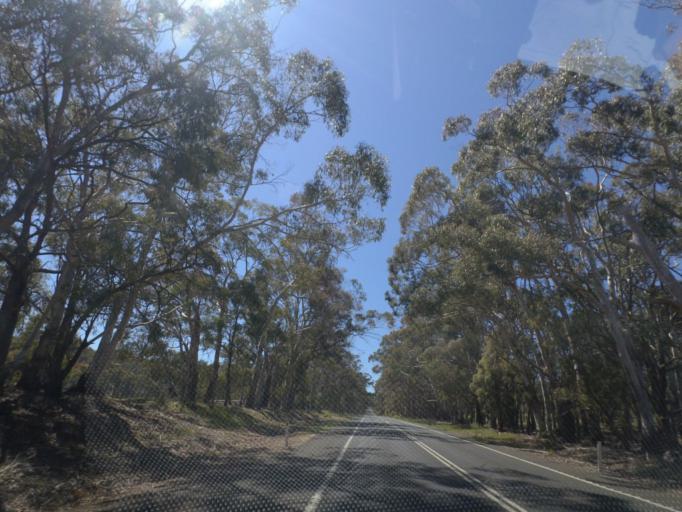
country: AU
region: Victoria
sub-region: Hume
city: Sunbury
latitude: -37.2411
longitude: 144.7375
